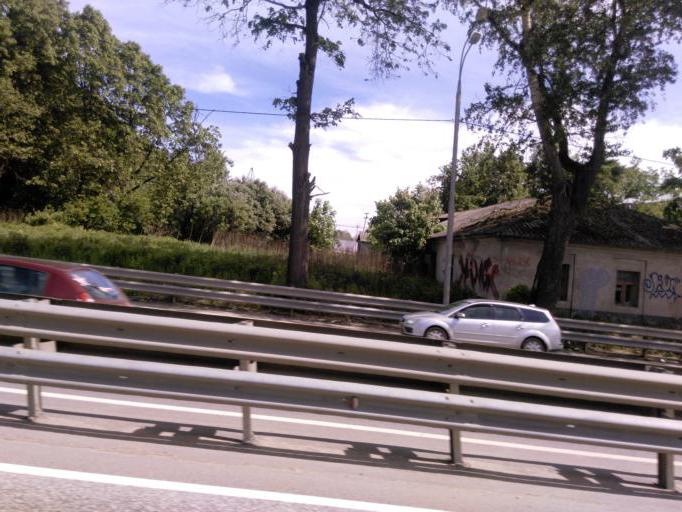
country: RU
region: Moskovskaya
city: Skhodnya
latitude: 55.9754
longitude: 37.3068
